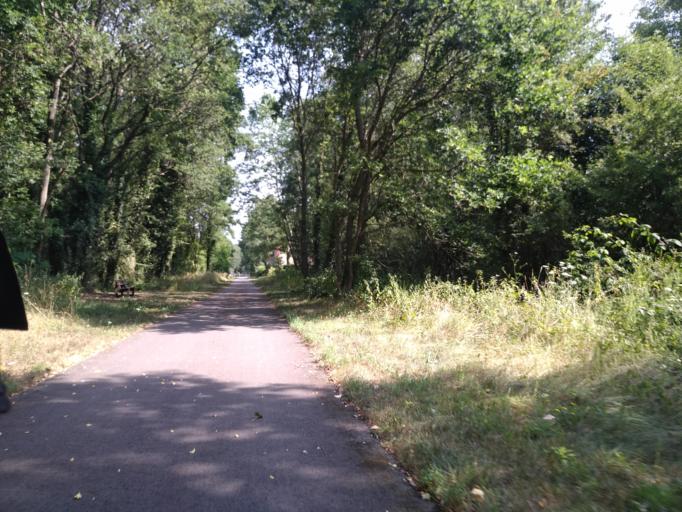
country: FR
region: Bourgogne
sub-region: Departement de Saone-et-Loire
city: Saint-Yan
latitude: 46.3465
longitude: 4.0284
